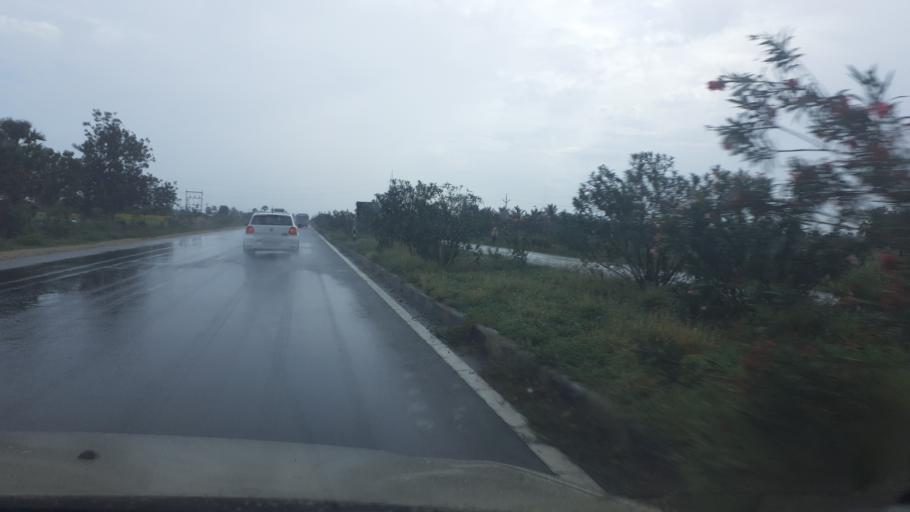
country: IN
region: Tamil Nadu
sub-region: Thoothukkudi
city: Kayattar
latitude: 8.9228
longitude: 77.7658
